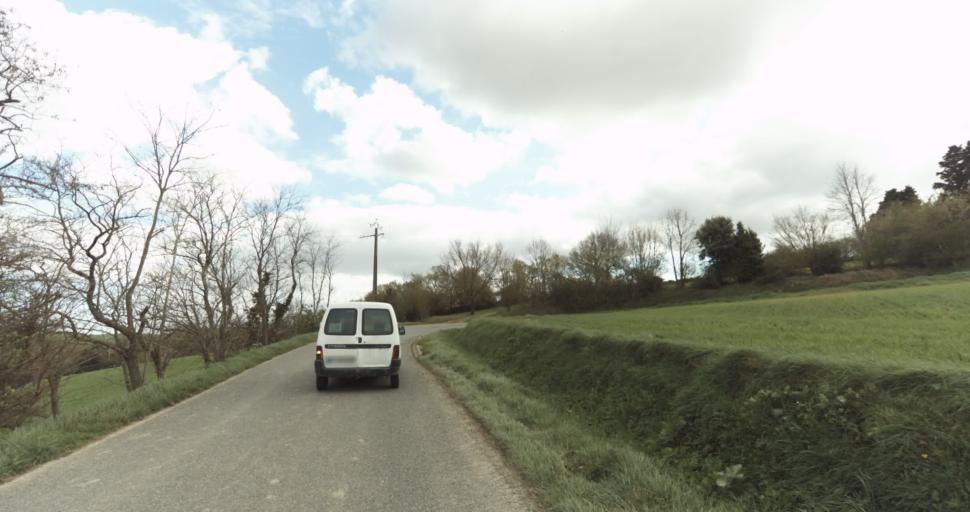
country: FR
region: Midi-Pyrenees
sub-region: Departement de la Haute-Garonne
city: Auterive
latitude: 43.3742
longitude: 1.4862
